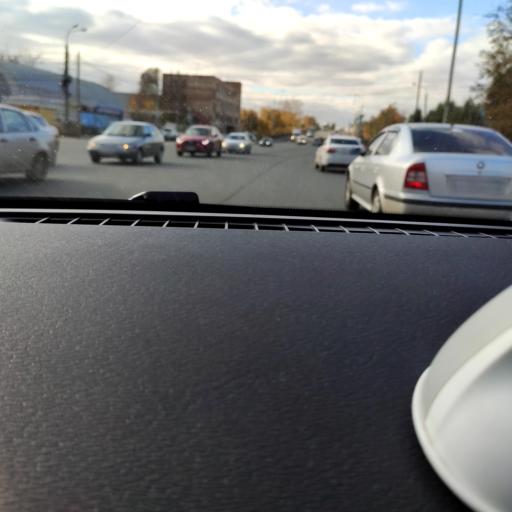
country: RU
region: Samara
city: Smyshlyayevka
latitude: 53.2272
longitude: 50.2903
